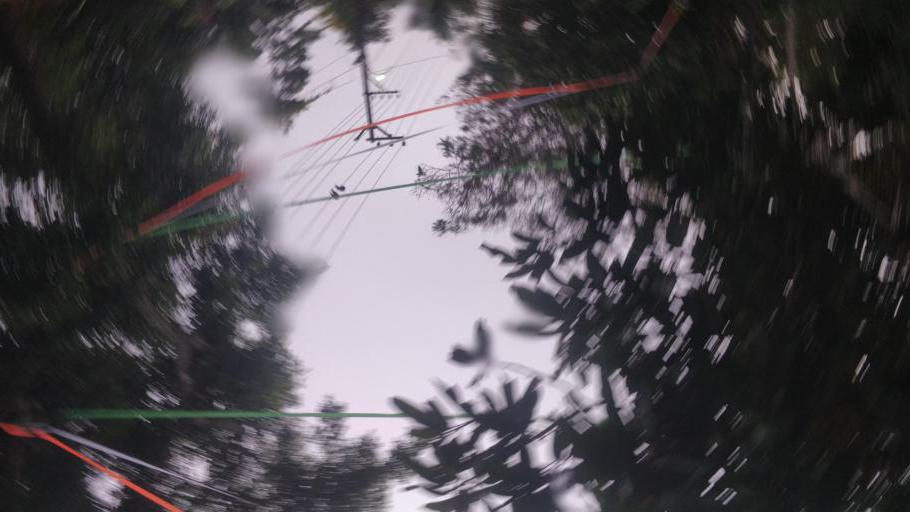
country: IN
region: Kerala
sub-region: Alappuzha
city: Shertallai
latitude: 9.6427
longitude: 76.3282
